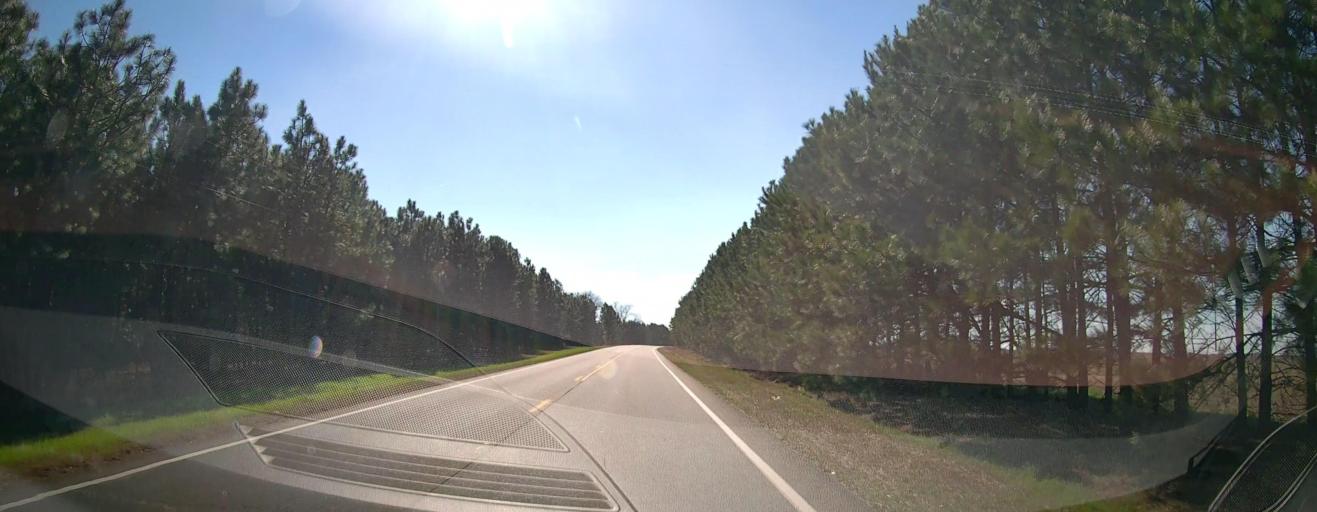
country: US
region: Georgia
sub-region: Macon County
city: Oglethorpe
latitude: 32.2131
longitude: -84.1123
